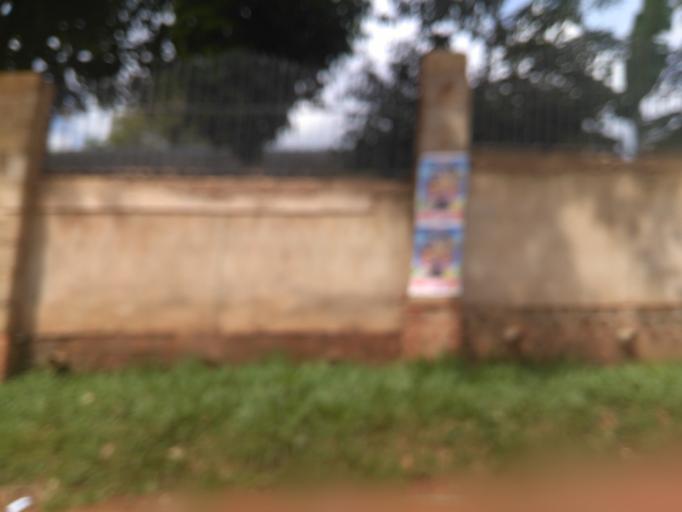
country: UG
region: Eastern Region
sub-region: Jinja District
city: Jinja
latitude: 0.4338
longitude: 33.2050
